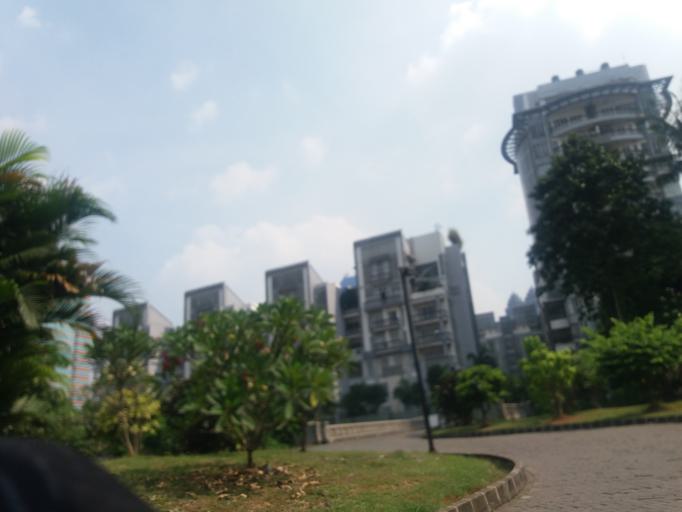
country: ID
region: Jakarta Raya
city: Jakarta
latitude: -6.2216
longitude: 106.8174
